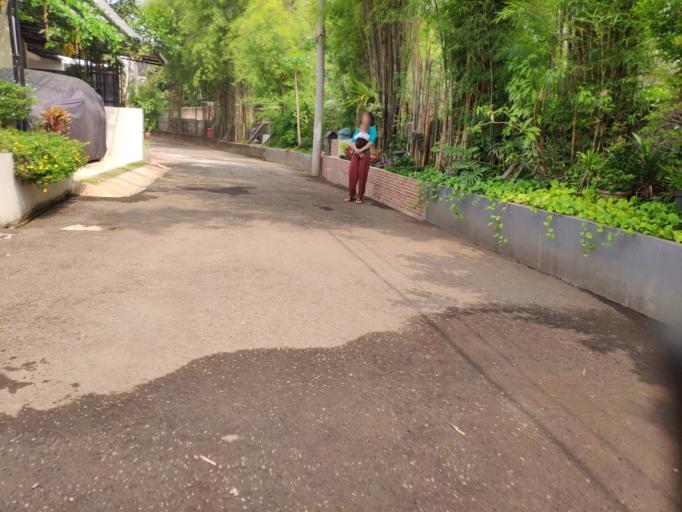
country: ID
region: West Java
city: Pamulang
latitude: -6.3238
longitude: 106.8058
